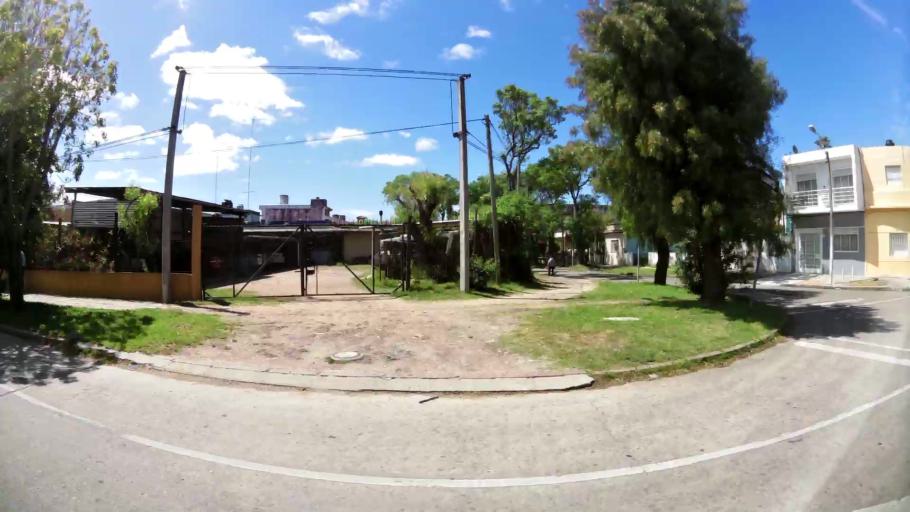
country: UY
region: Montevideo
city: Montevideo
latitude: -34.8554
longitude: -56.1359
